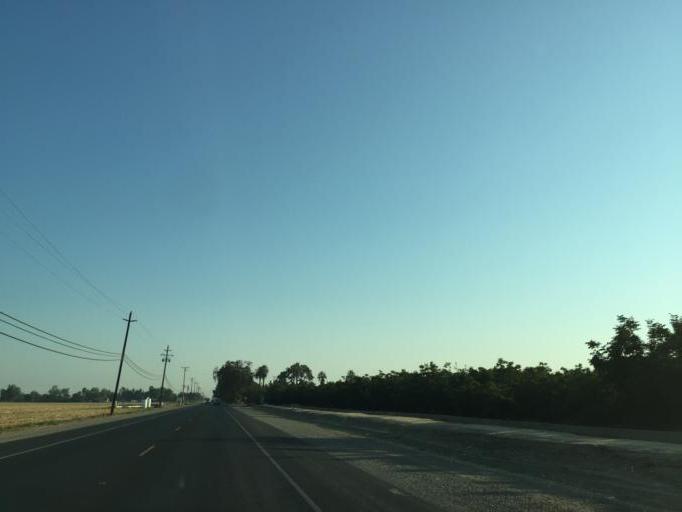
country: US
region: California
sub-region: Tulare County
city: Visalia
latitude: 36.3974
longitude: -119.2963
